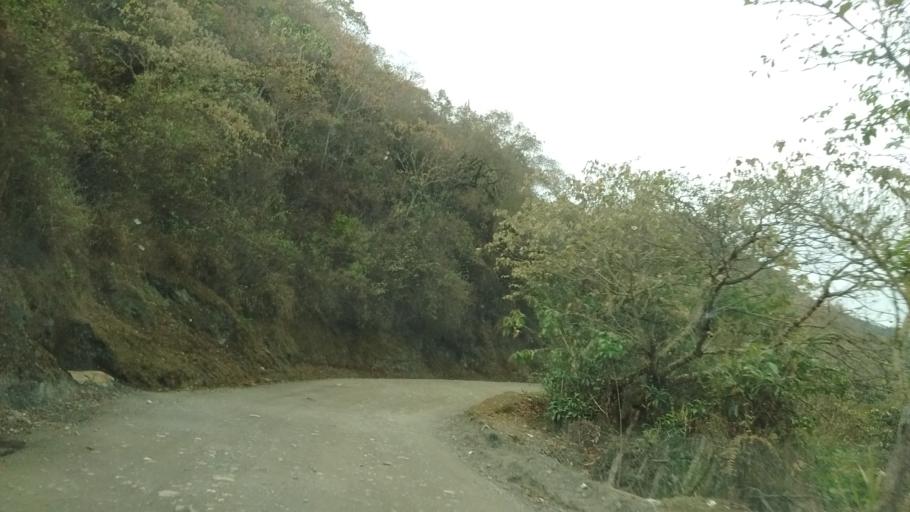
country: CO
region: Cauca
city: Almaguer
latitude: 1.8614
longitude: -76.9338
